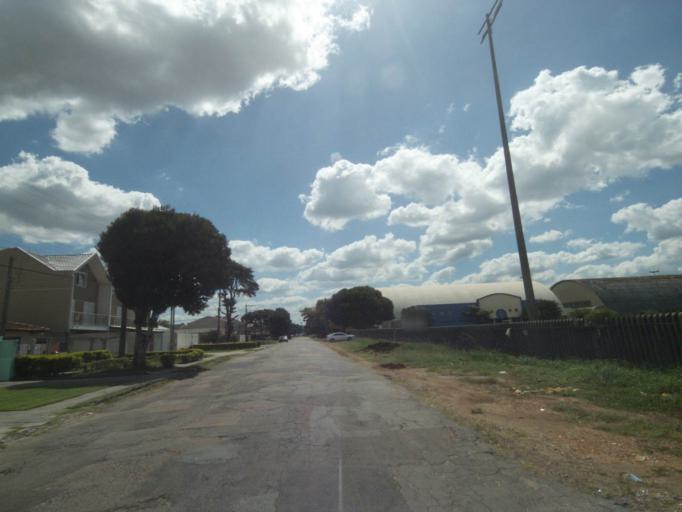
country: BR
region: Parana
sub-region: Pinhais
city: Pinhais
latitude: -25.4363
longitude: -49.2079
